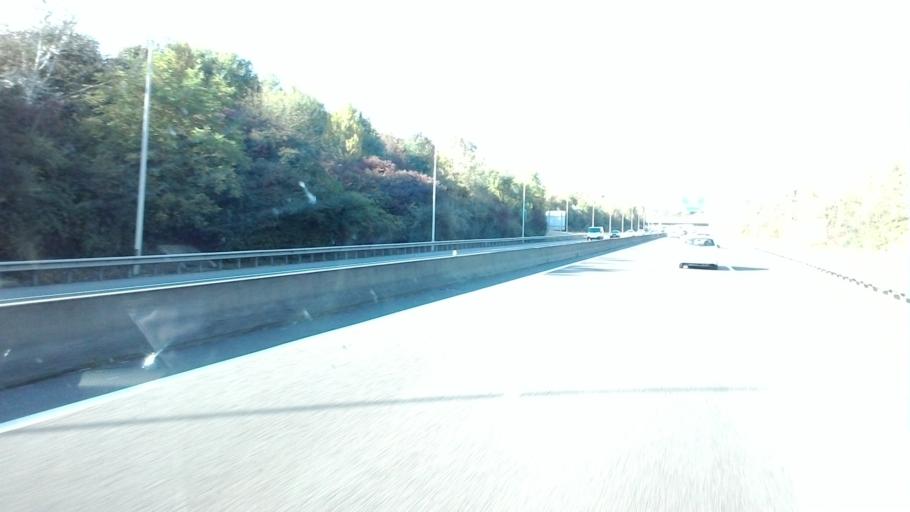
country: LU
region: Luxembourg
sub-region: Canton de Luxembourg
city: Strassen
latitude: 49.6132
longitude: 6.0826
